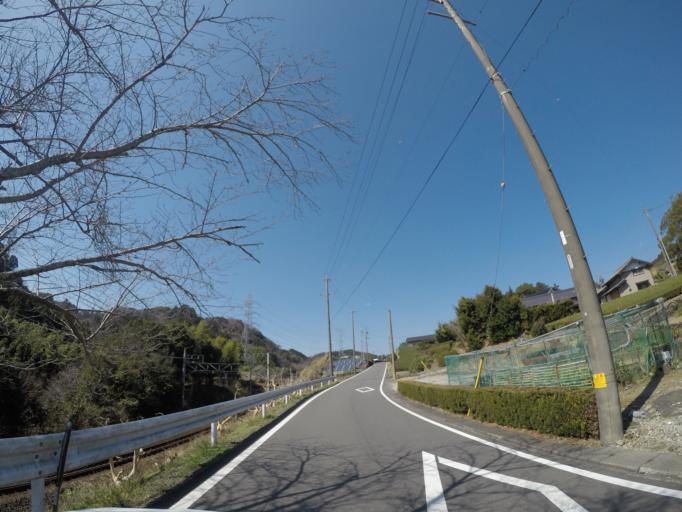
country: JP
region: Shizuoka
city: Kanaya
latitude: 34.7942
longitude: 138.1256
